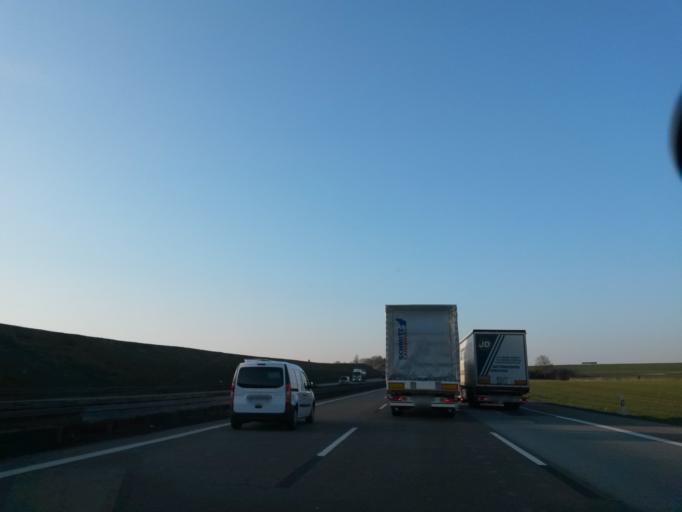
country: DE
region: Bavaria
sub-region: Upper Bavaria
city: Stammham
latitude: 48.8469
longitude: 11.4659
